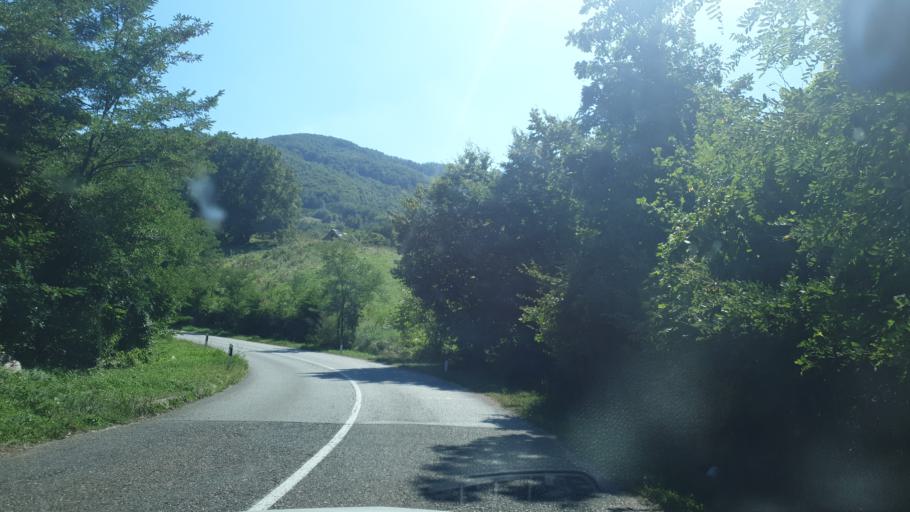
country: RS
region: Central Serbia
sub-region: Kolubarski Okrug
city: Mionica
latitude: 44.1579
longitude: 19.9888
